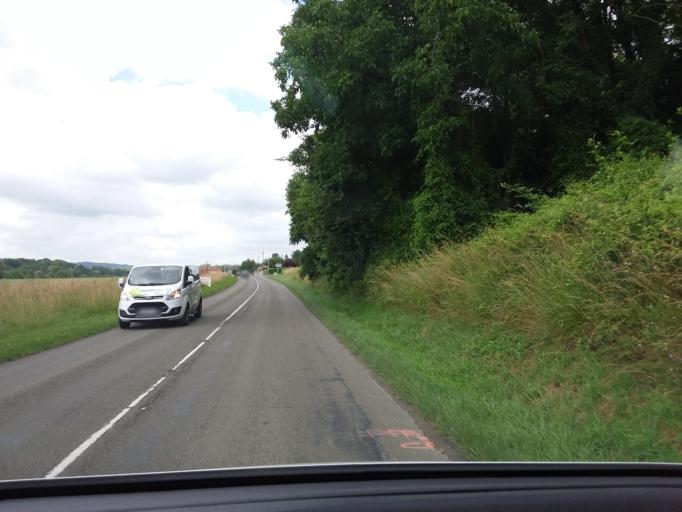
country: FR
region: Picardie
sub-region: Departement de l'Aisne
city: Vailly-sur-Aisne
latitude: 49.4065
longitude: 3.4889
